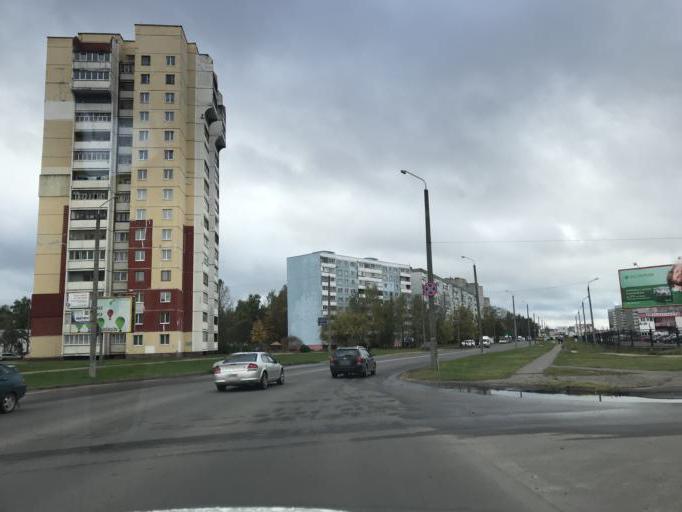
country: BY
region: Mogilev
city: Mahilyow
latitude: 53.8794
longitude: 30.3692
